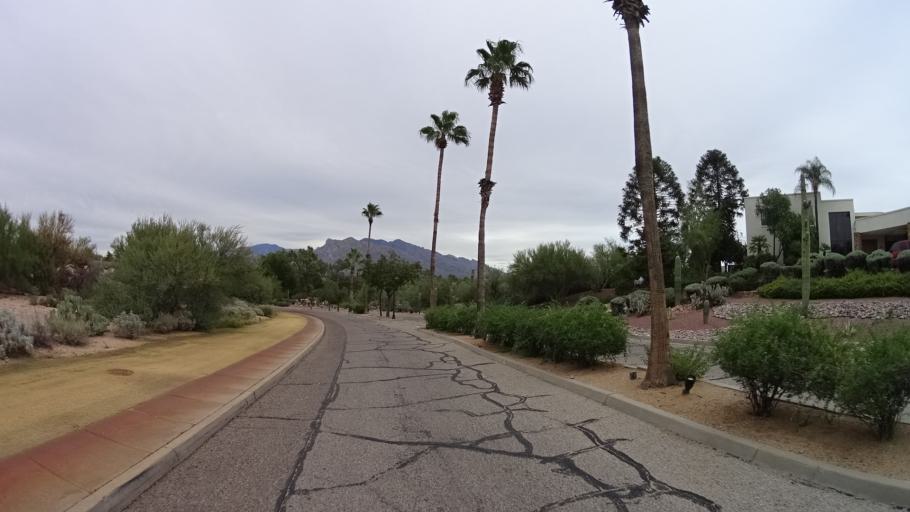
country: US
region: Arizona
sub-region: Pima County
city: Casas Adobes
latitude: 32.3586
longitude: -111.0276
